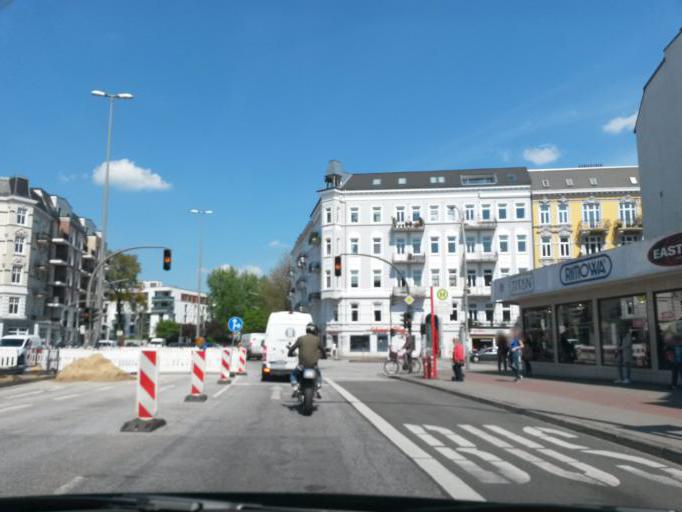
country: DE
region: Hamburg
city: St. Pauli
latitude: 53.5742
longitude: 9.9593
